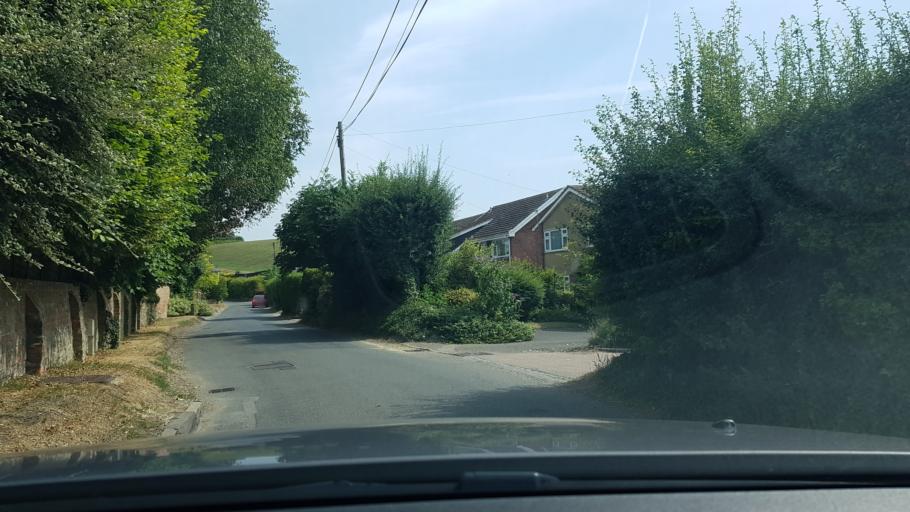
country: GB
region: England
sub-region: West Berkshire
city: Lambourn
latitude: 51.5106
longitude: -1.5259
